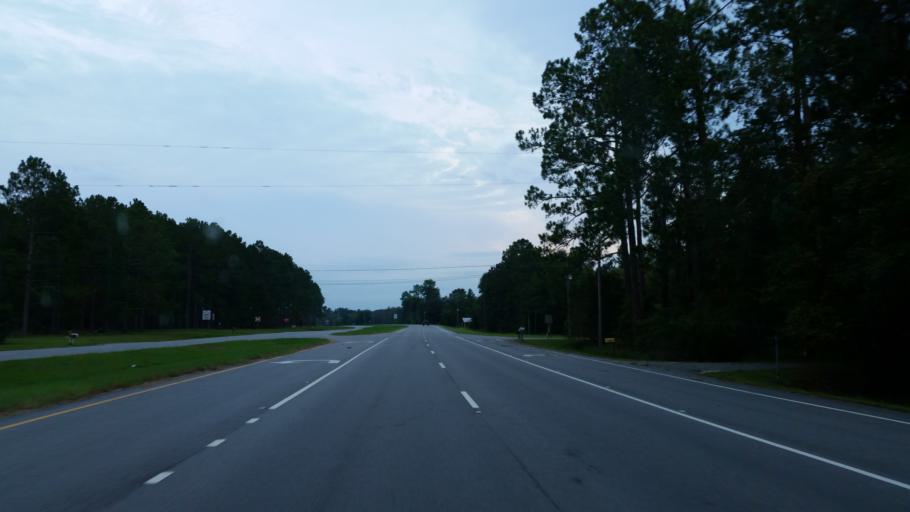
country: US
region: Georgia
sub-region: Lowndes County
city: Valdosta
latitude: 30.7348
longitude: -83.2206
